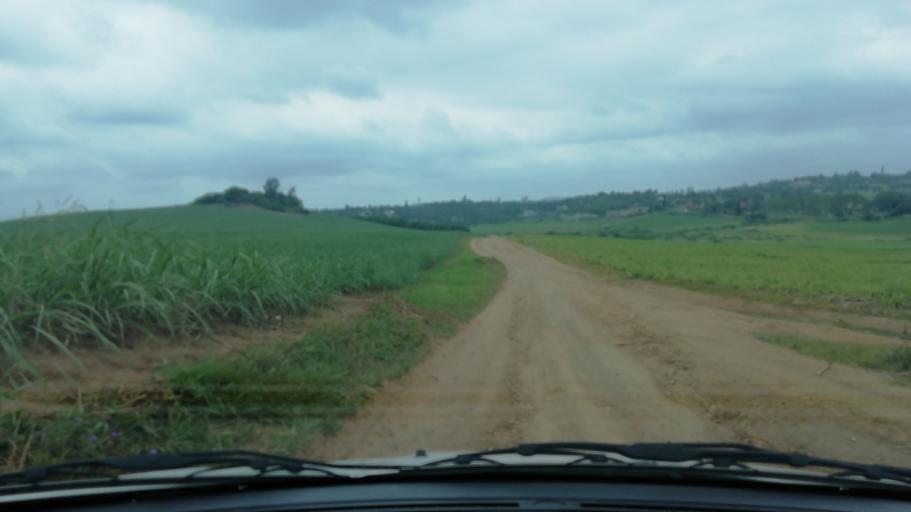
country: ZA
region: KwaZulu-Natal
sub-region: uThungulu District Municipality
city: Empangeni
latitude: -28.7323
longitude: 31.9081
